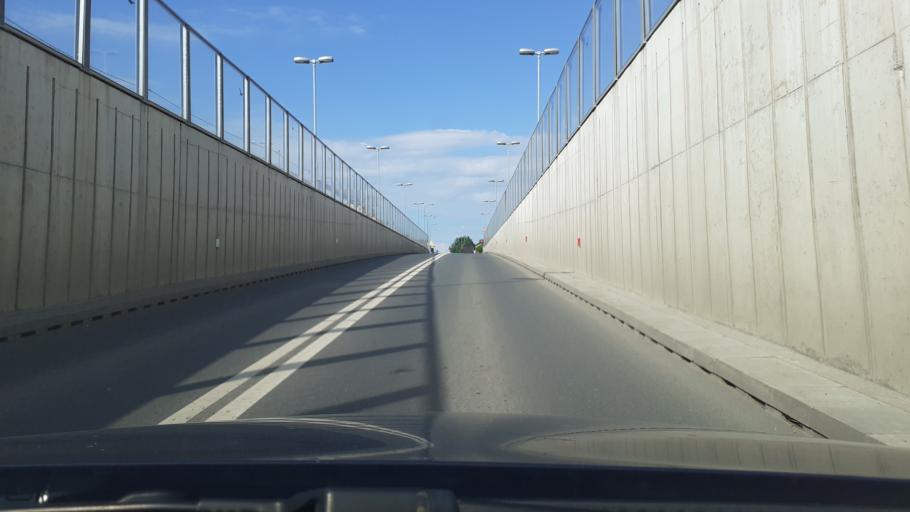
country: HR
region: Brodsko-Posavska
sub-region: Grad Slavonski Brod
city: Slavonski Brod
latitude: 45.1626
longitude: 18.0336
